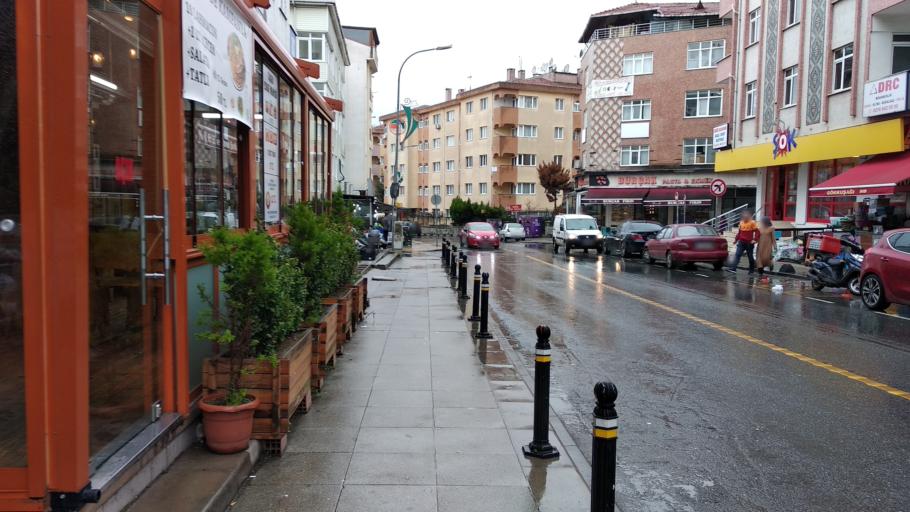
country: TR
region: Istanbul
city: Samandira
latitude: 41.0216
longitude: 29.1922
